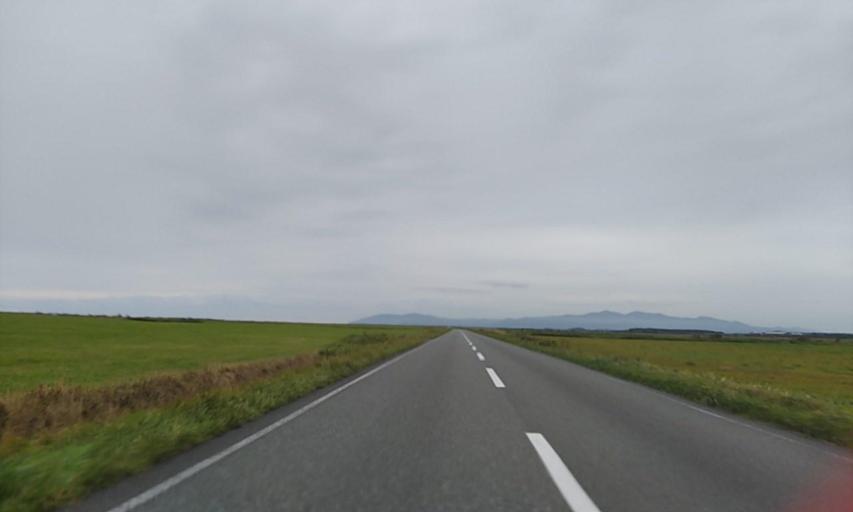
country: JP
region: Hokkaido
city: Makubetsu
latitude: 45.2098
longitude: 142.2902
